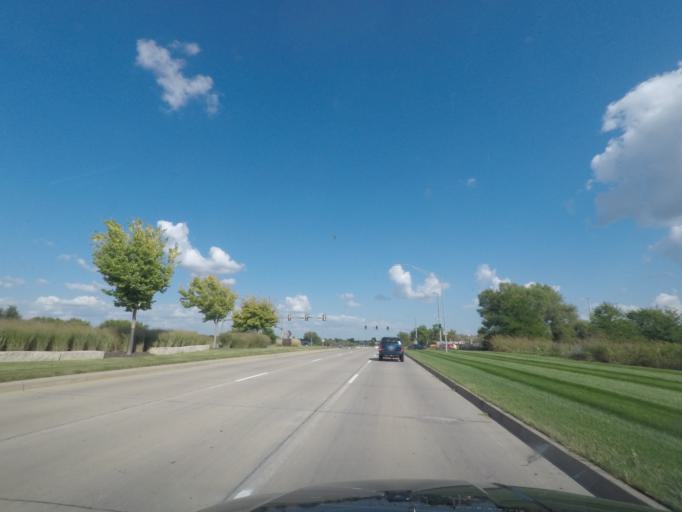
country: US
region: Iowa
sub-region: Dallas County
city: Waukee
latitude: 41.5733
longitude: -93.8072
